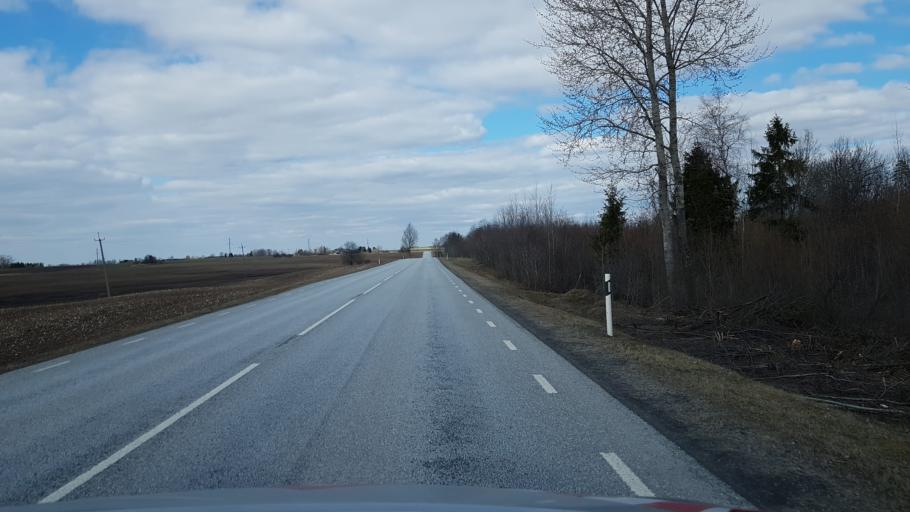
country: EE
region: Laeaene-Virumaa
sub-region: Rakke vald
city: Rakke
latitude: 58.9403
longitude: 26.2777
